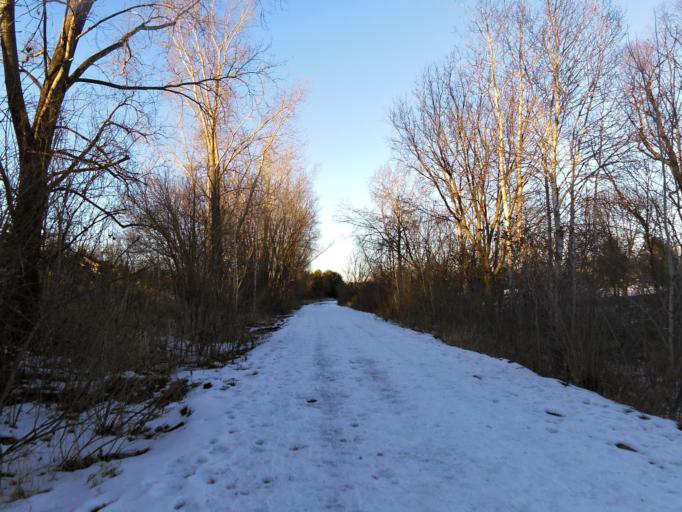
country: US
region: Minnesota
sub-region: Washington County
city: Stillwater
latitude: 45.0734
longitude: -92.8350
